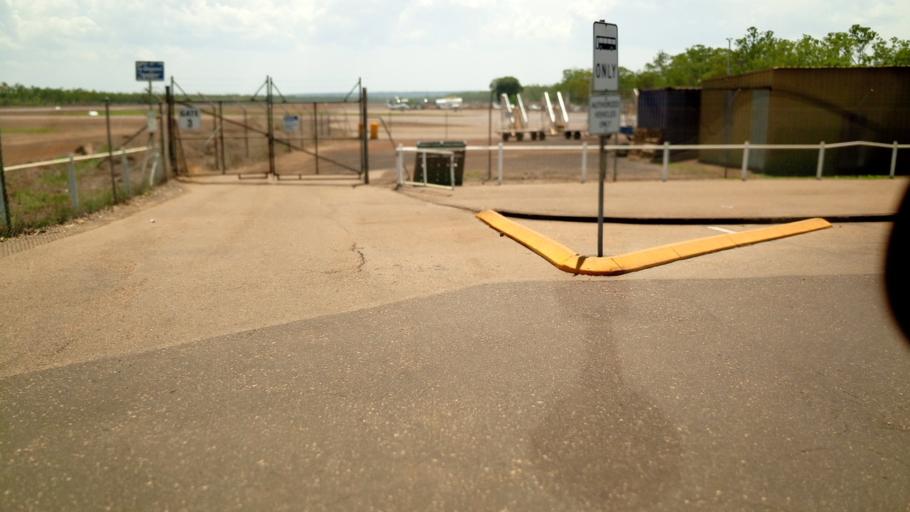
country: AU
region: Northern Territory
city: Alyangula
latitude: -13.9732
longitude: 136.4574
